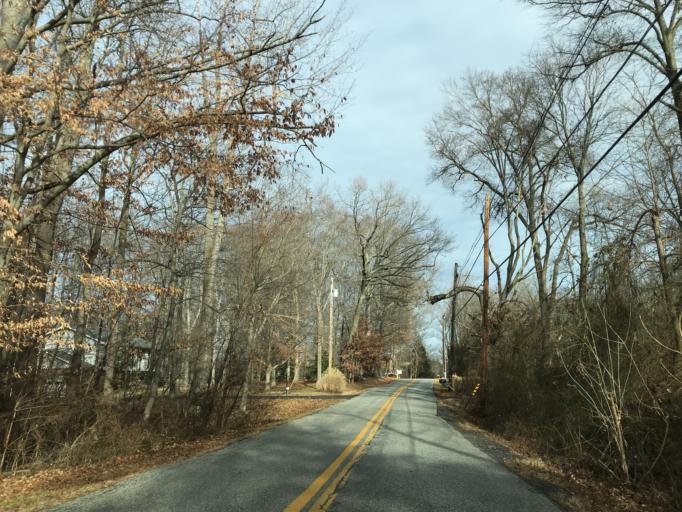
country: US
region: Maryland
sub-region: Baltimore County
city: Kingsville
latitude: 39.4443
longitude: -76.3930
